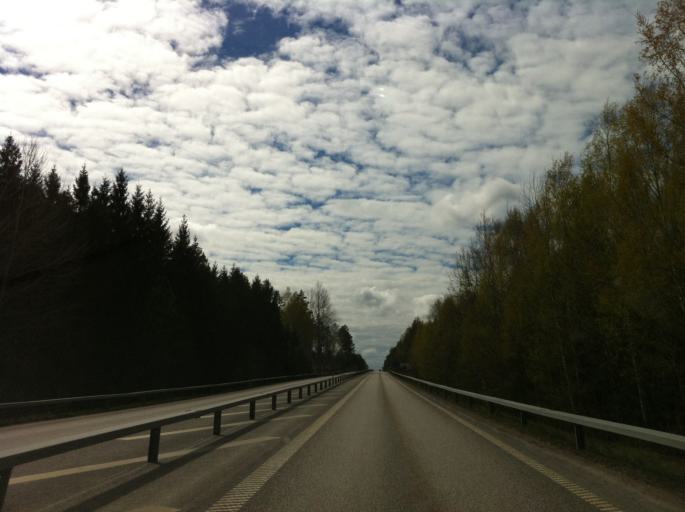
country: SE
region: OEstergoetland
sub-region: Valdemarsviks Kommun
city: Valdemarsvik
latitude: 58.1736
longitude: 16.5673
